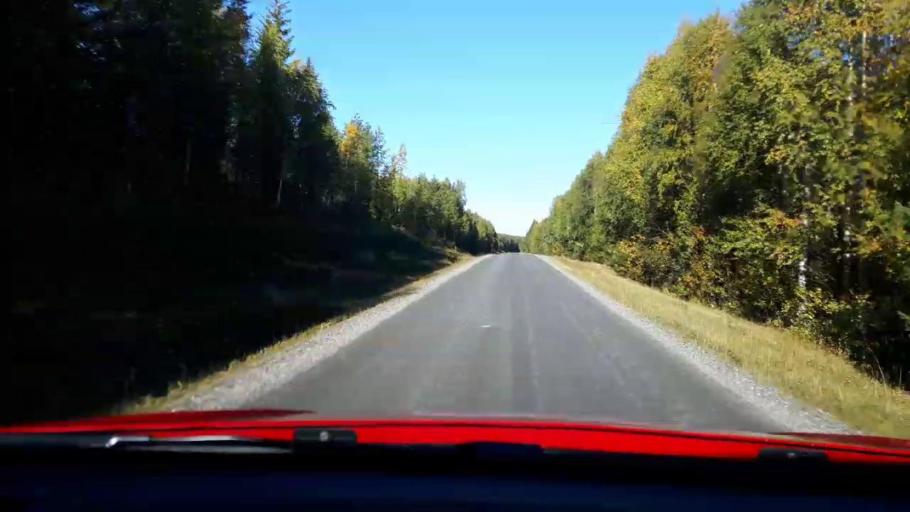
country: NO
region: Nord-Trondelag
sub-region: Lierne
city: Sandvika
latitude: 64.5346
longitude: 14.0225
